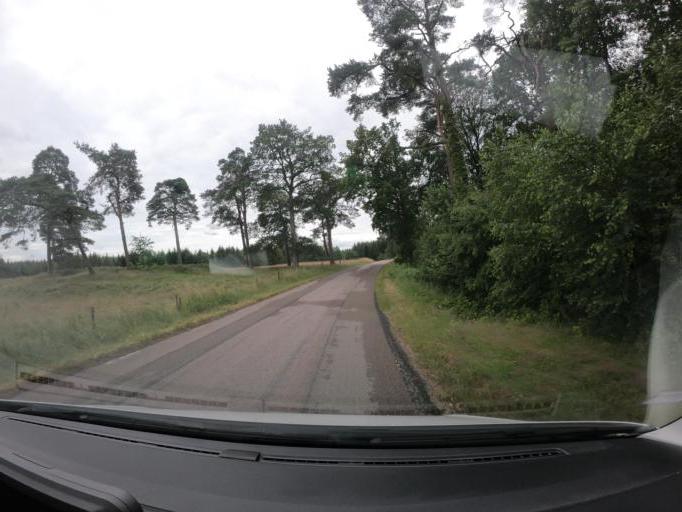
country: SE
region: Skane
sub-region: Angelholms Kommun
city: Munka-Ljungby
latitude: 56.2995
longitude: 13.0801
